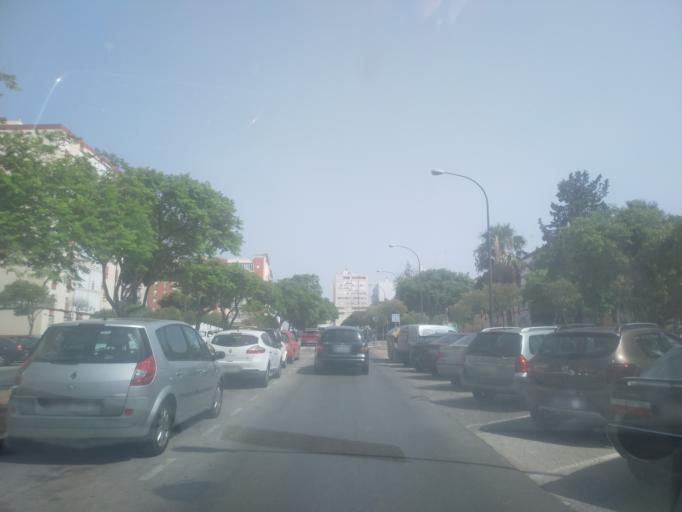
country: ES
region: Andalusia
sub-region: Provincia de Cadiz
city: San Fernando
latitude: 36.4711
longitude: -6.2012
